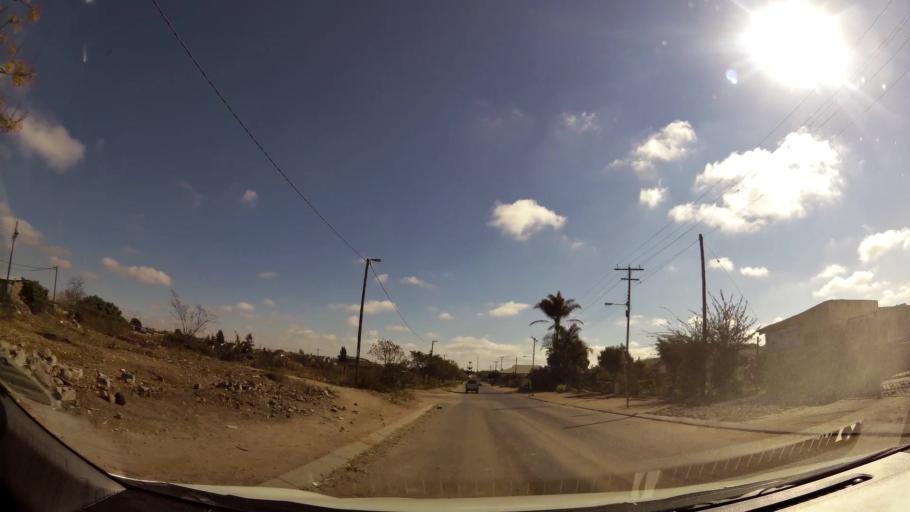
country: ZA
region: Limpopo
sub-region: Capricorn District Municipality
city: Polokwane
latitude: -23.8632
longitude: 29.3850
